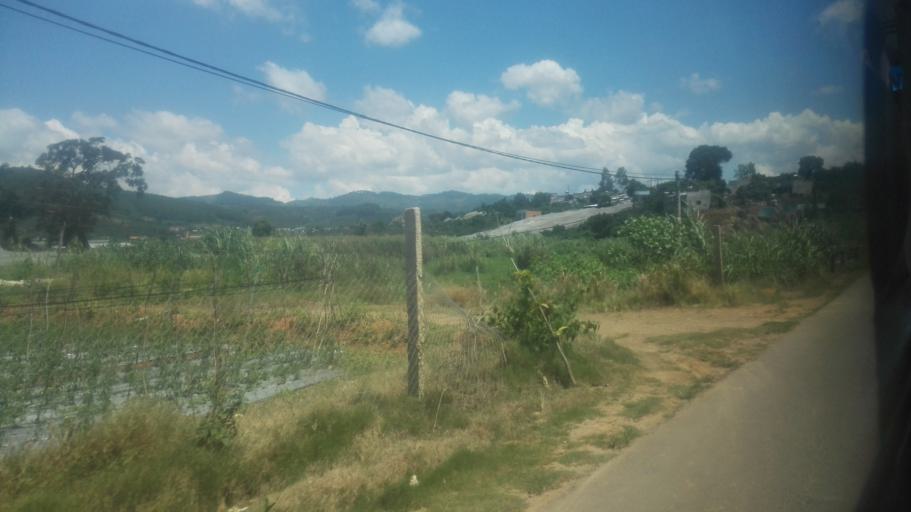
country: VN
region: Lam Dong
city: Da Lat
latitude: 11.8756
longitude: 108.3420
